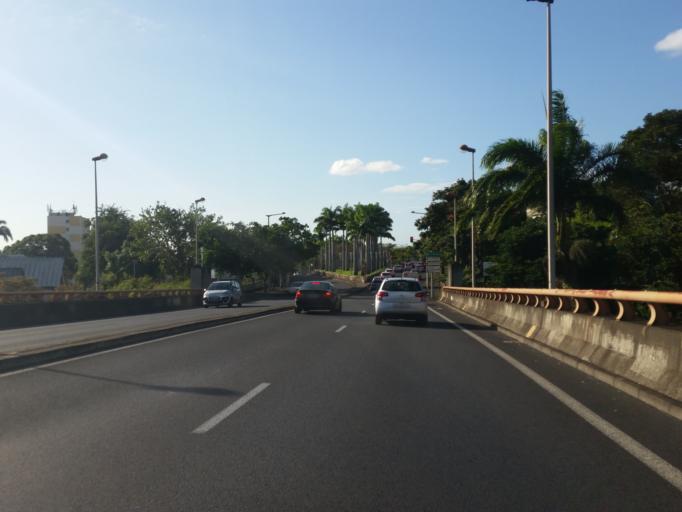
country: RE
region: Reunion
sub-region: Reunion
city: Saint-Denis
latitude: -20.8881
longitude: 55.4436
